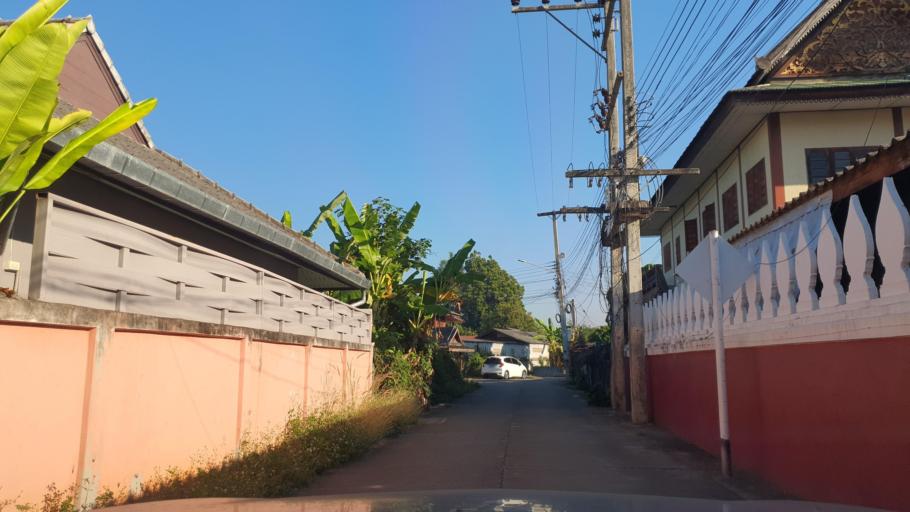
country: TH
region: Chiang Mai
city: Hang Dong
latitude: 18.6931
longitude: 98.9515
